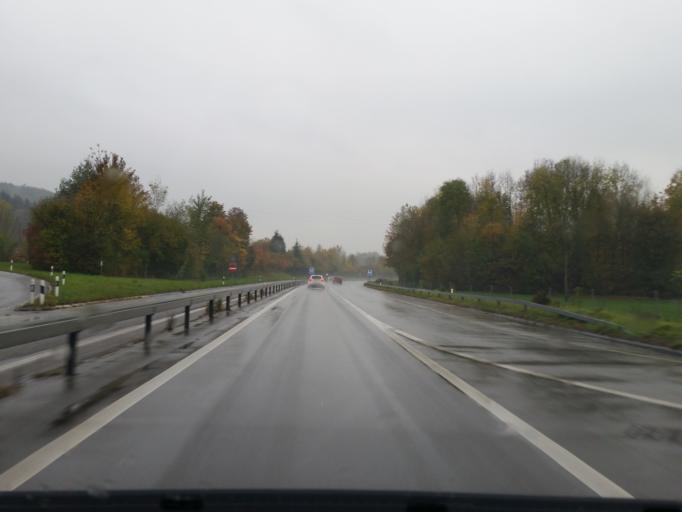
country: CH
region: Thurgau
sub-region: Weinfelden District
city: Wigoltingen
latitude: 47.5815
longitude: 9.0269
